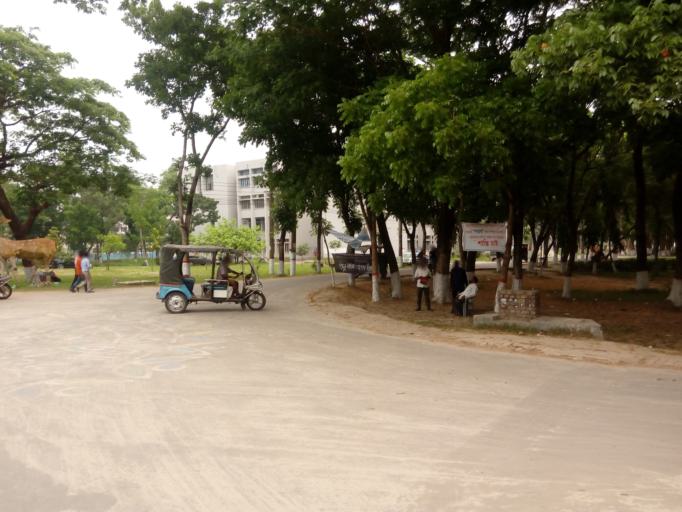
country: BD
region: Khulna
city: Khulna
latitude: 22.8019
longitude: 89.5340
